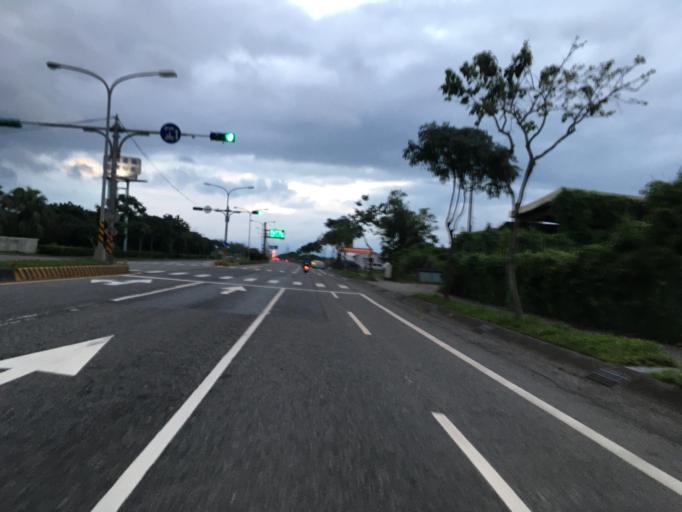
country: TW
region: Taiwan
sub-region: Yilan
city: Yilan
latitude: 24.6150
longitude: 121.8493
